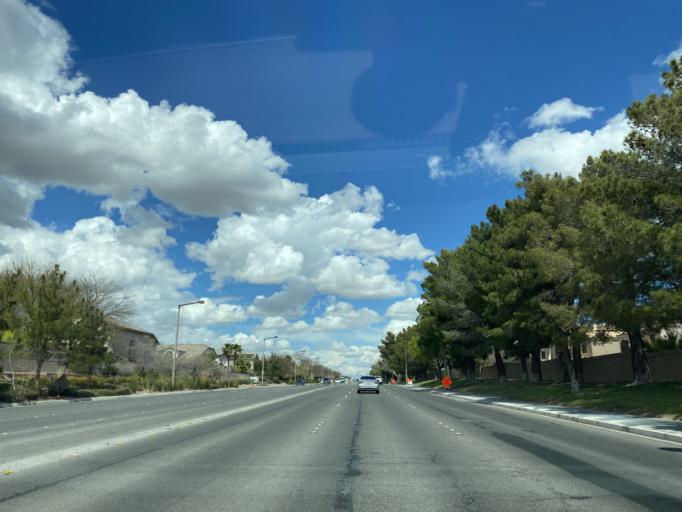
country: US
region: Nevada
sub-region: Clark County
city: Summerlin South
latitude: 36.1388
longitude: -115.3153
